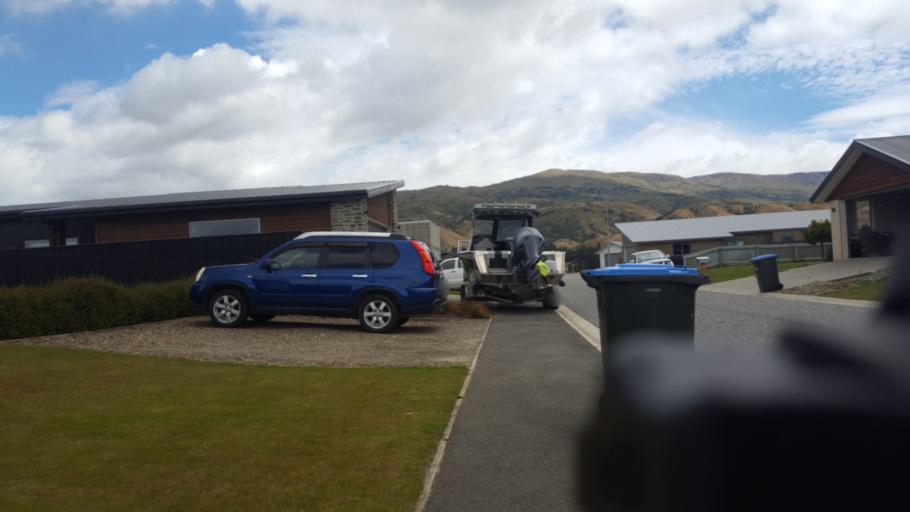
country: NZ
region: Otago
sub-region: Queenstown-Lakes District
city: Wanaka
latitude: -45.0458
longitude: 169.1803
